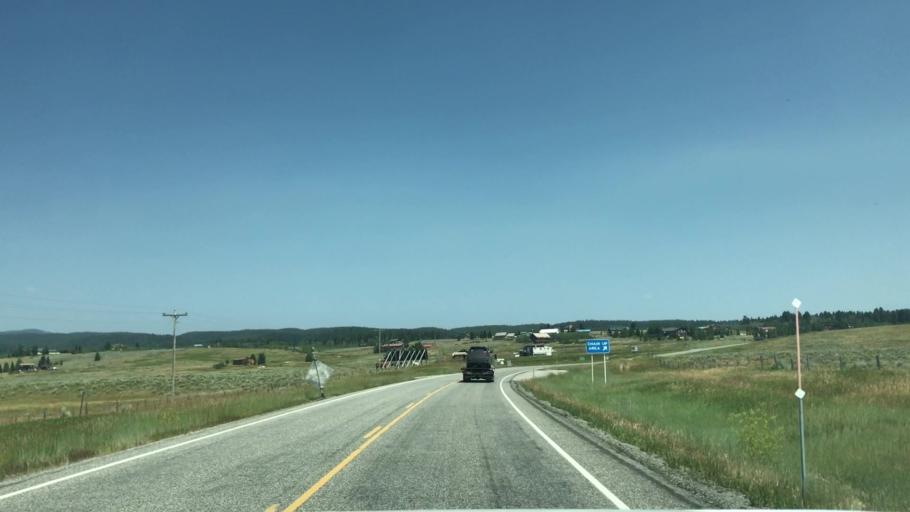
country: US
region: Montana
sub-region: Gallatin County
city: West Yellowstone
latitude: 44.7854
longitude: -111.1133
